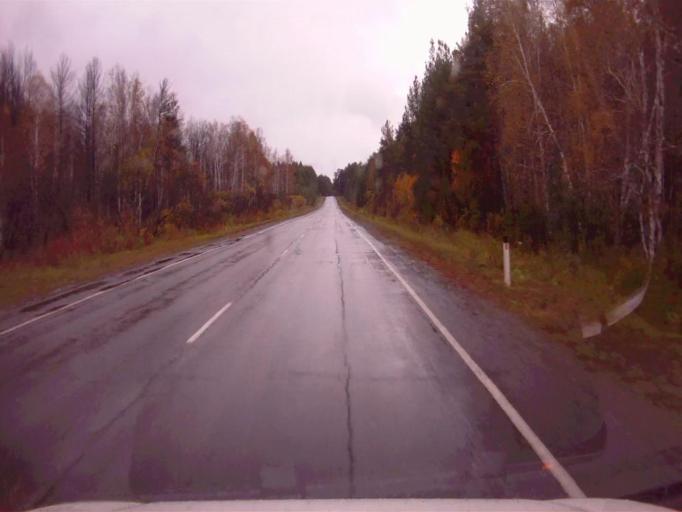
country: RU
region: Chelyabinsk
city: Verkhniy Ufaley
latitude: 56.0178
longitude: 60.3069
